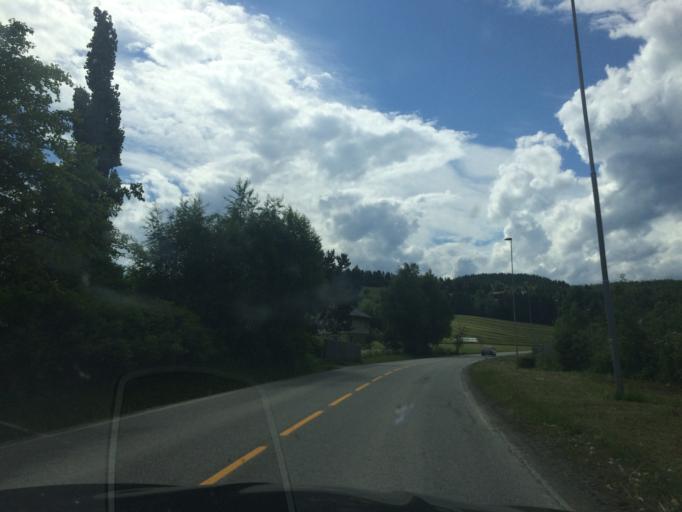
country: NO
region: Sor-Trondelag
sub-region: Selbu
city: Mebonden
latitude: 63.2414
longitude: 11.0838
